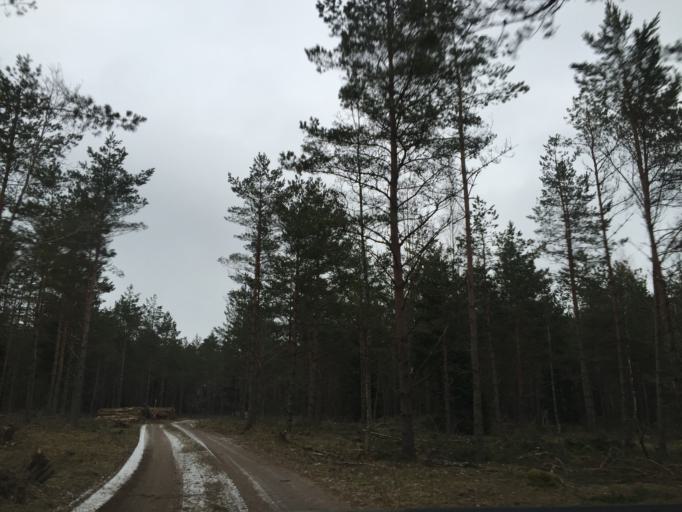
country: EE
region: Saare
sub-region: Kuressaare linn
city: Kuressaare
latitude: 58.3890
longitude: 22.2596
